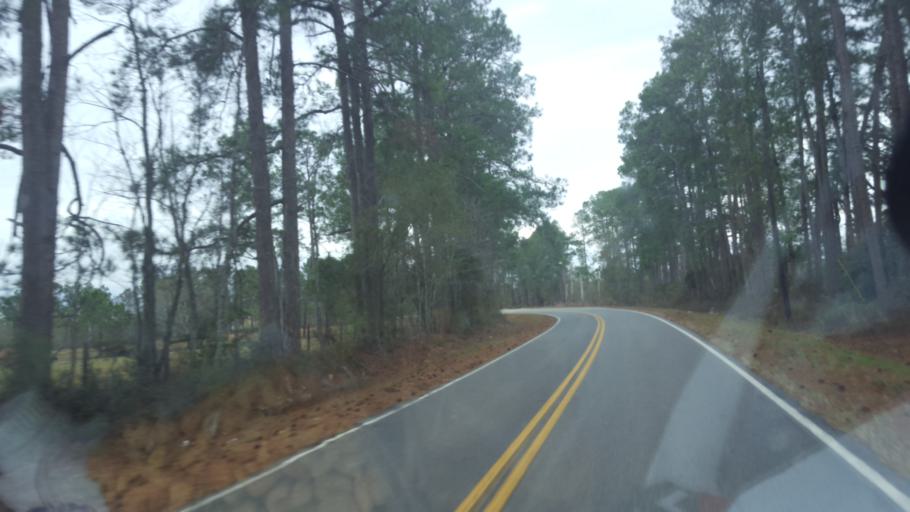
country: US
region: Georgia
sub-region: Wilcox County
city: Rochelle
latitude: 31.8113
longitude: -83.4613
